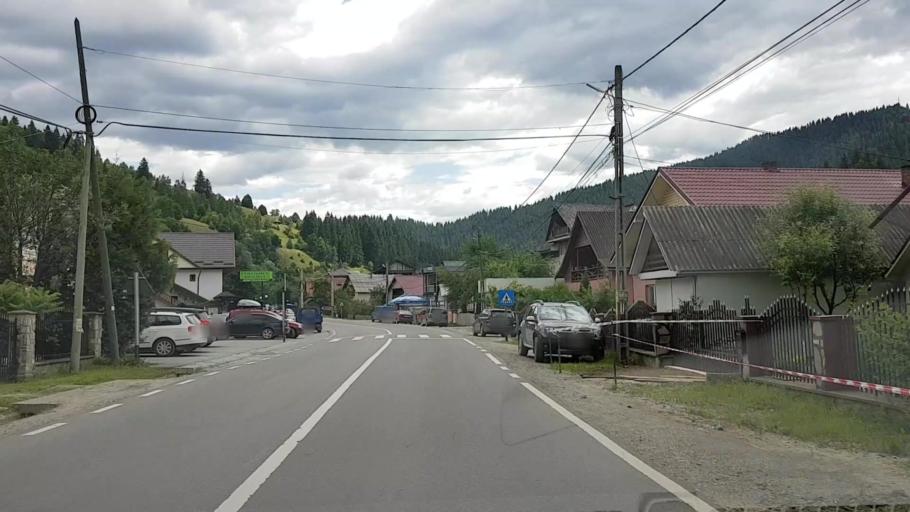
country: RO
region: Neamt
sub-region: Comuna Farcasa
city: Farcasa
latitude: 47.1570
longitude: 25.8370
